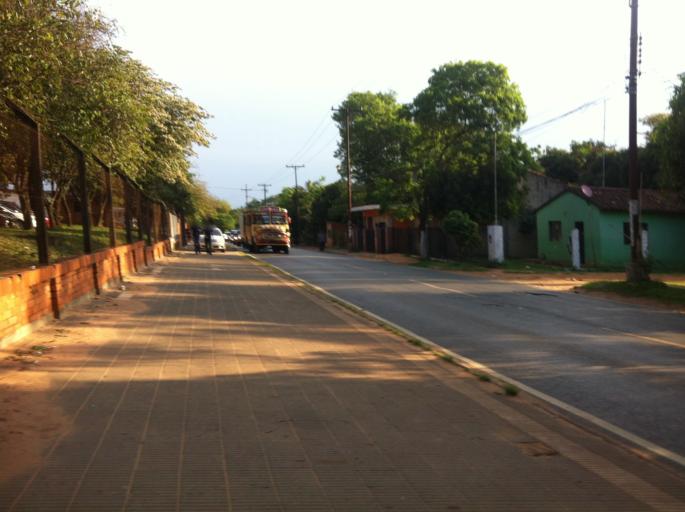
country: PY
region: Central
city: San Lorenzo
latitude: -25.2948
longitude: -57.4916
